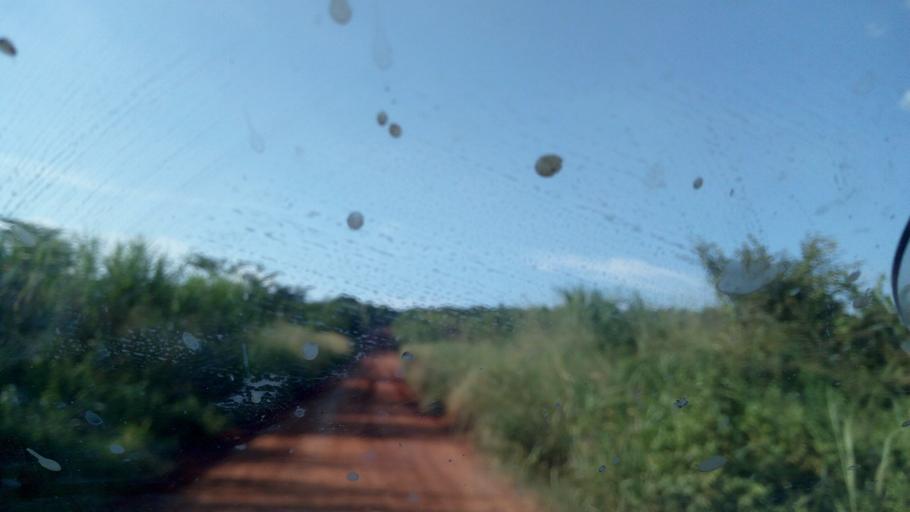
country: BI
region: Bururi
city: Rumonge
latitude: -4.2322
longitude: 28.9912
